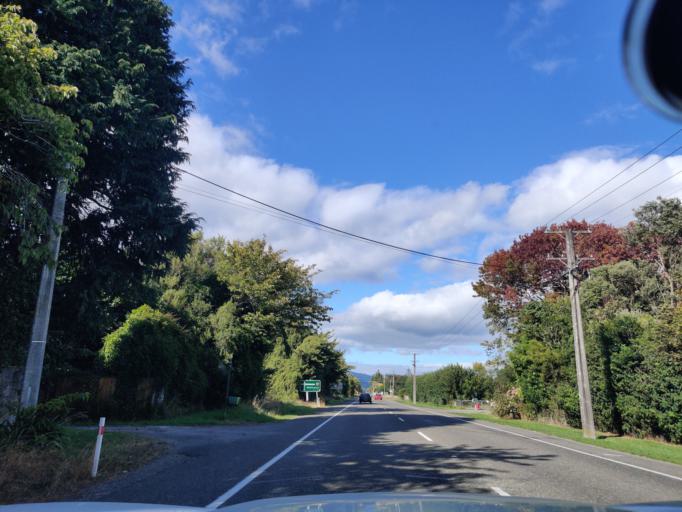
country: NZ
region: Manawatu-Wanganui
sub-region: Horowhenua District
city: Levin
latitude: -40.6531
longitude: 175.2839
